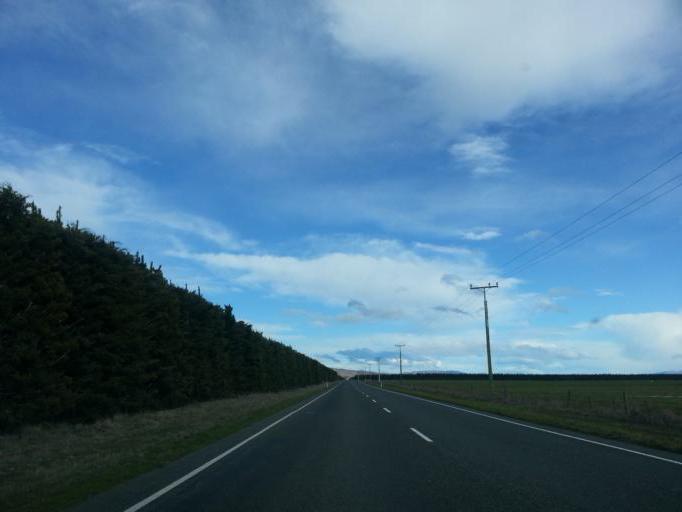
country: NZ
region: Canterbury
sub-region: Hurunui District
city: Amberley
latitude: -42.8066
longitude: 172.8221
